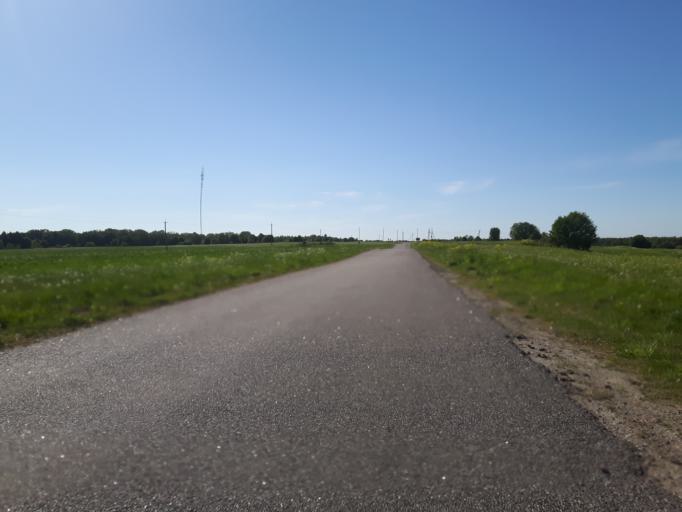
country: EE
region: Laeaene-Virumaa
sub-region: Haljala vald
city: Haljala
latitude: 59.5462
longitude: 26.1409
